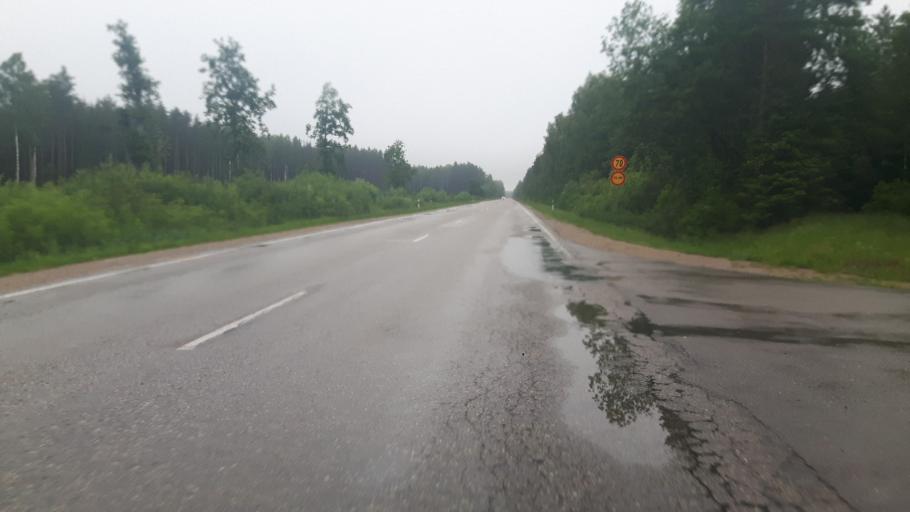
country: LV
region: Rucavas
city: Rucava
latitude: 56.1149
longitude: 21.1421
